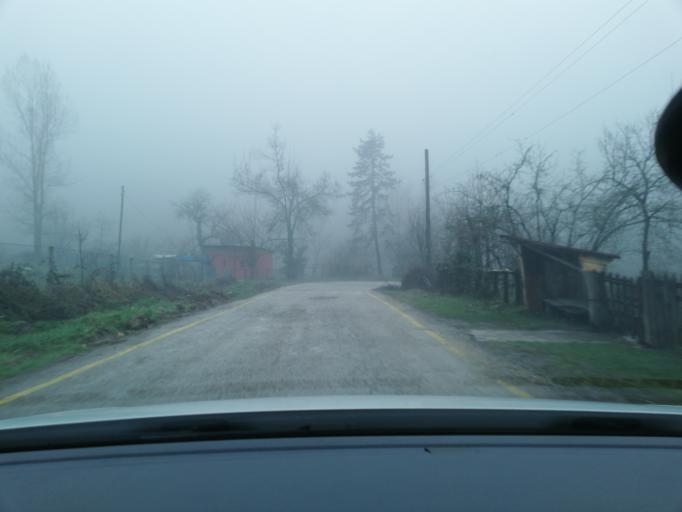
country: TR
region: Duzce
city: Kaynasli
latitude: 40.7591
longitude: 31.3747
